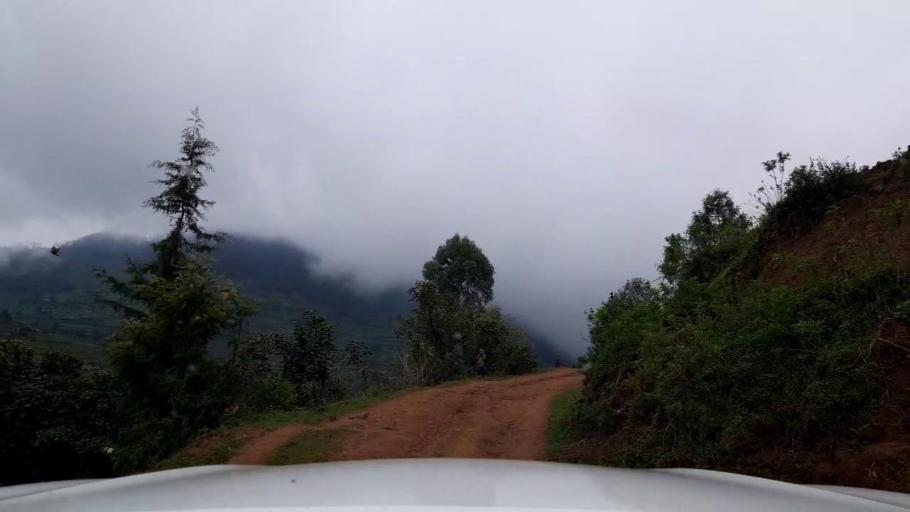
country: RW
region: Northern Province
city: Musanze
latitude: -1.5939
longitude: 29.7873
